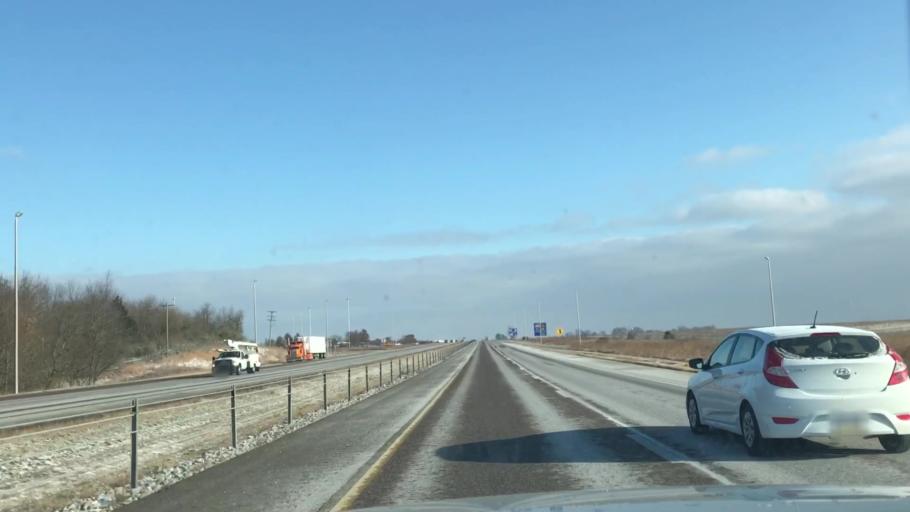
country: US
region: Illinois
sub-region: Madison County
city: Worden
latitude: 38.8673
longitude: -89.8533
